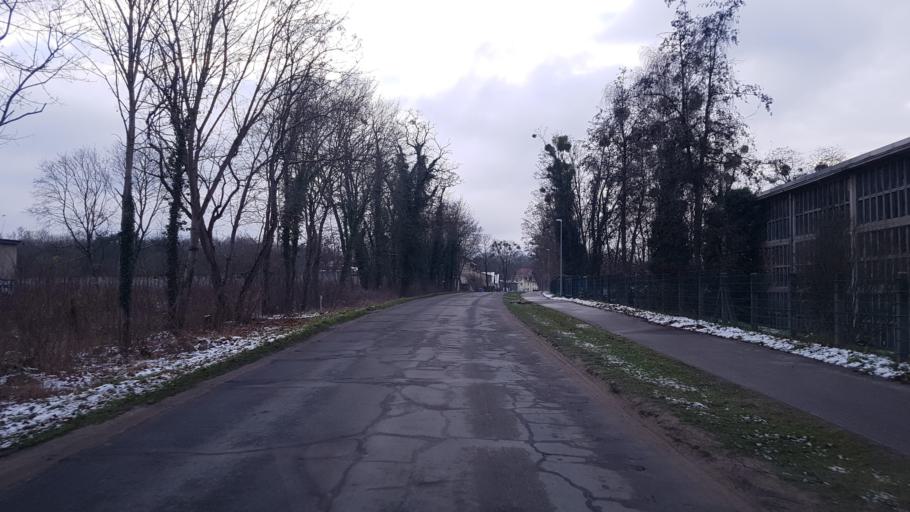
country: DE
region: Brandenburg
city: Petershagen
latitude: 52.4954
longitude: 13.8213
